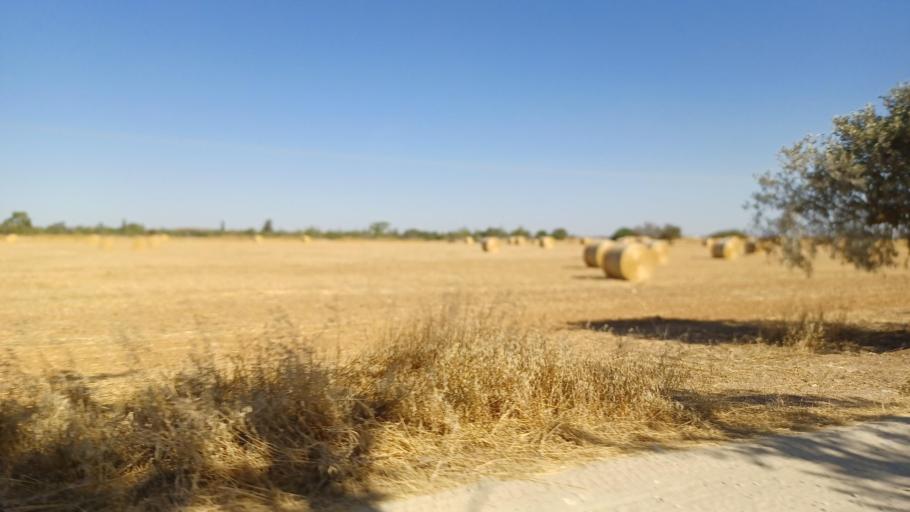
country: CY
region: Larnaka
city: Pergamos
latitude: 35.0430
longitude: 33.7034
